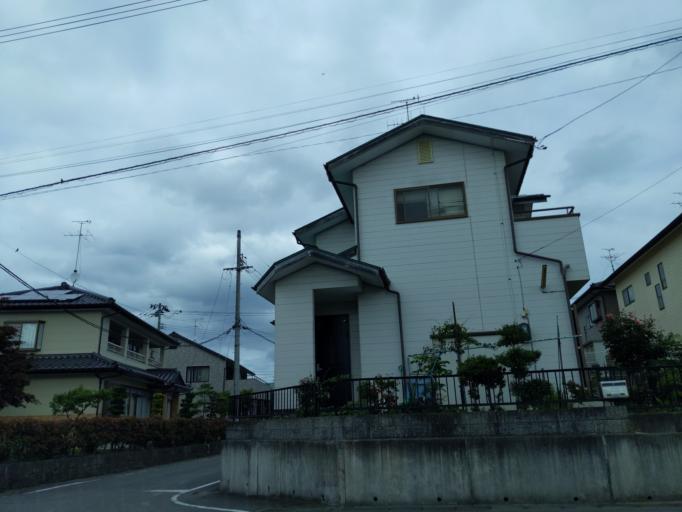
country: JP
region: Fukushima
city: Sukagawa
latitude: 37.2978
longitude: 140.3888
